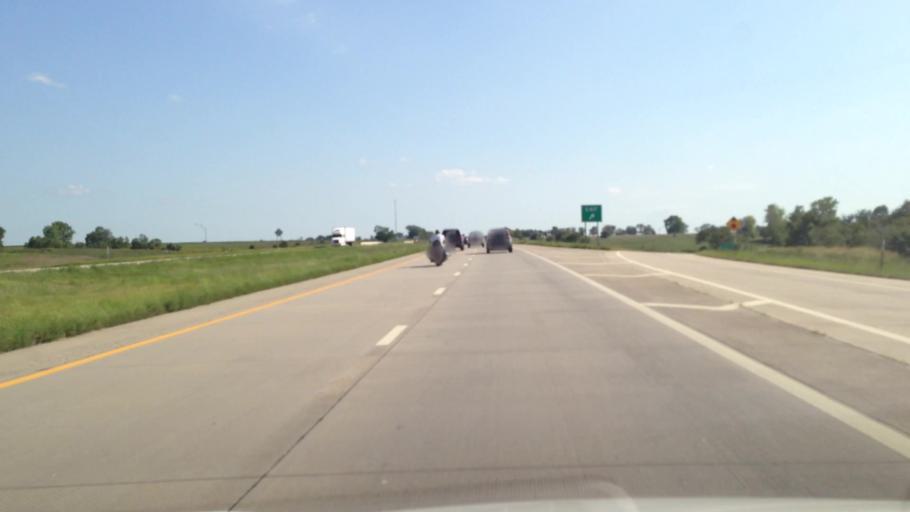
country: US
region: Kansas
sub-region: Bourbon County
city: Fort Scott
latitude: 37.9965
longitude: -94.7051
